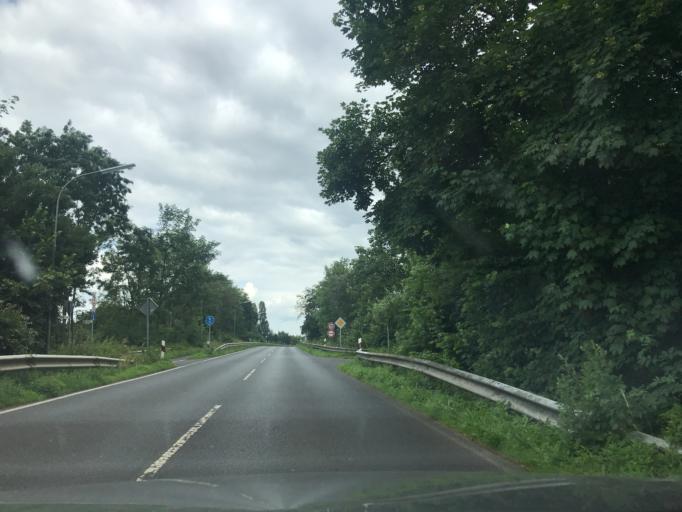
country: DE
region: North Rhine-Westphalia
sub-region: Regierungsbezirk Dusseldorf
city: Neubrueck
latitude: 51.1695
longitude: 6.6509
